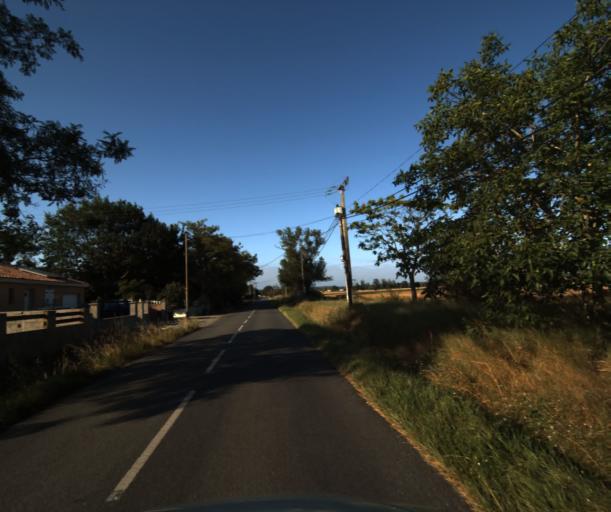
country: FR
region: Midi-Pyrenees
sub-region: Departement de la Haute-Garonne
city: Muret
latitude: 43.4586
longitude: 1.3725
